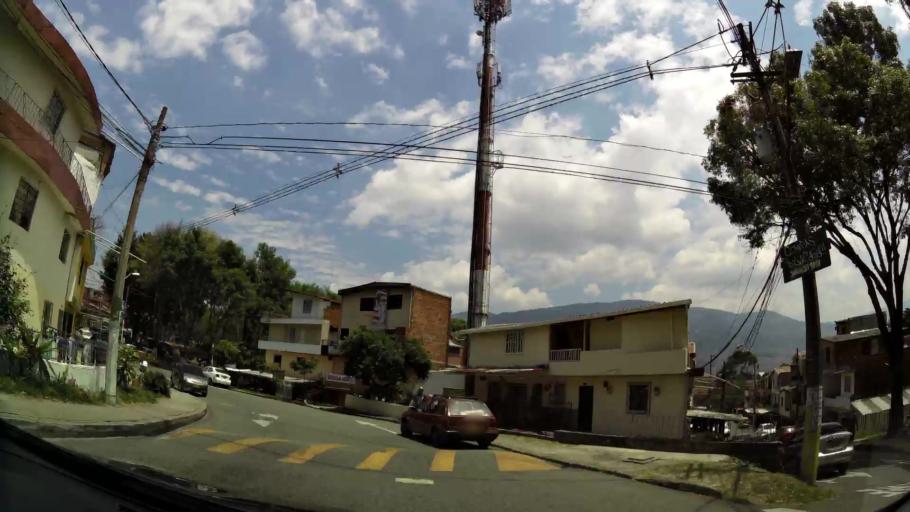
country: CO
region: Antioquia
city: Bello
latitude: 6.2995
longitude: -75.5743
